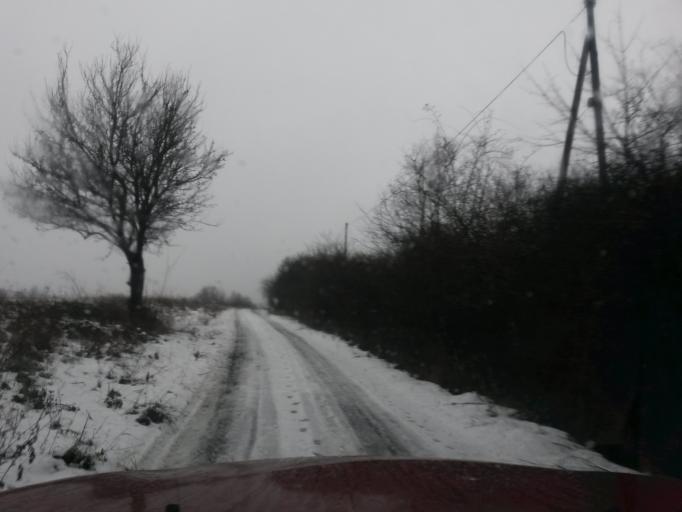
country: SK
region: Presovsky
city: Stropkov
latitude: 49.2514
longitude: 21.7505
